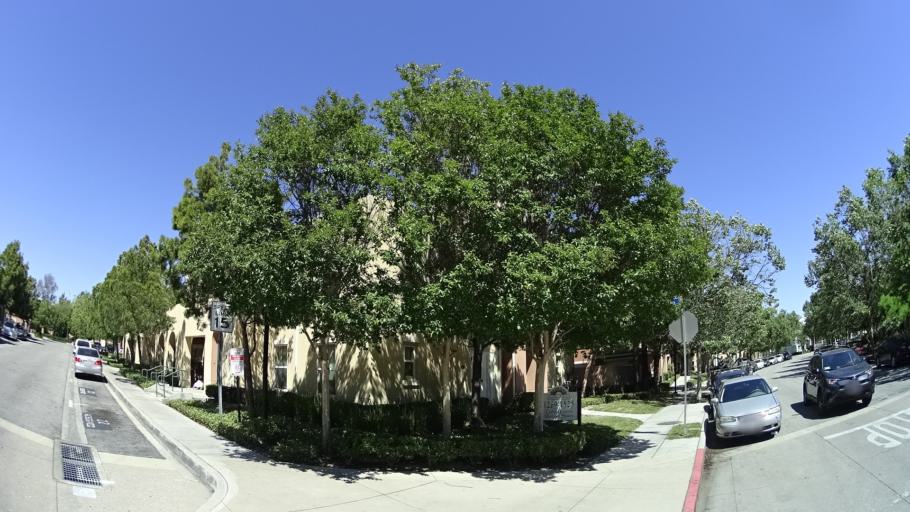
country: US
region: California
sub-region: Los Angeles County
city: Los Angeles
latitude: 34.0506
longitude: -118.2252
